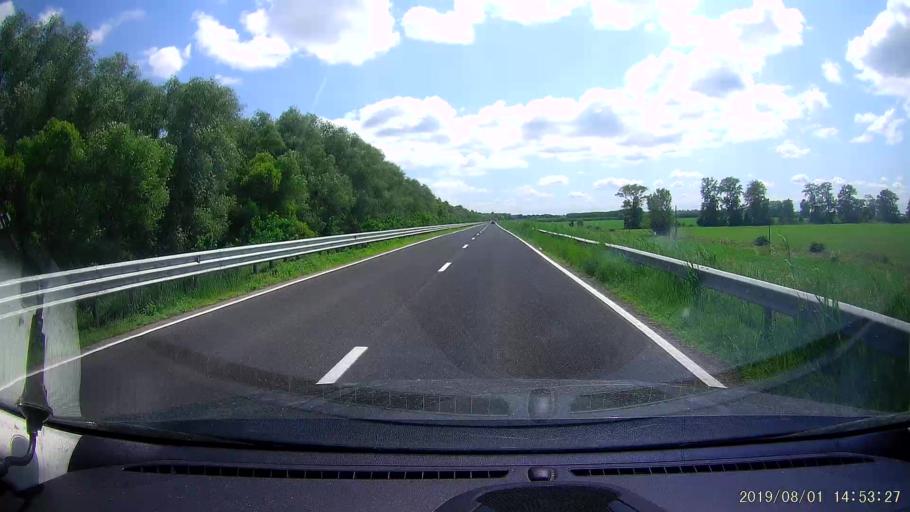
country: RO
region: Braila
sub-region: Municipiul Braila
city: Braila
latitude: 45.3351
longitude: 28.0026
